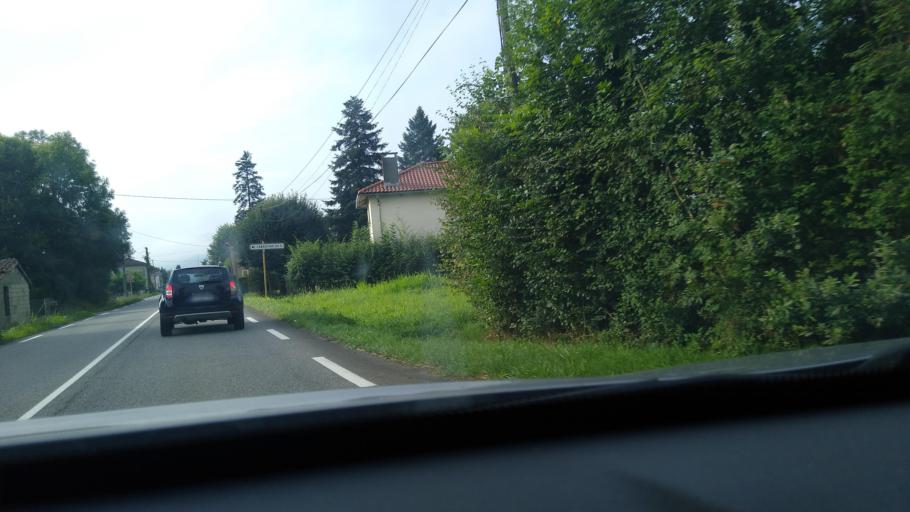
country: FR
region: Midi-Pyrenees
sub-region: Departement de la Haute-Garonne
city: Salies-du-Salat
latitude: 43.0568
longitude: 0.9777
